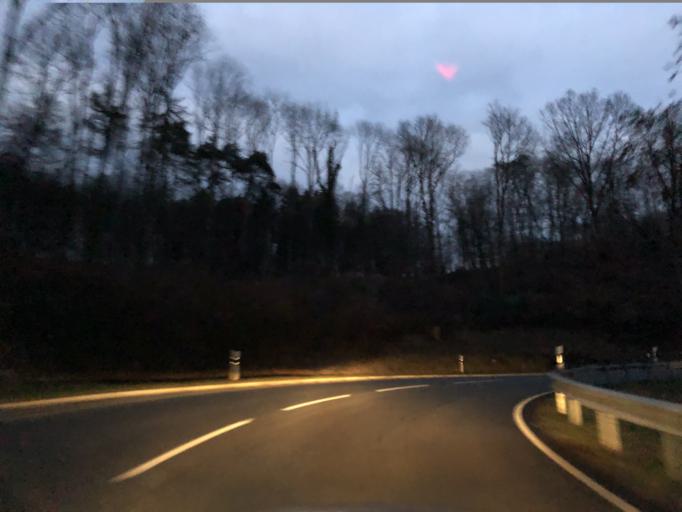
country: DE
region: Rheinland-Pfalz
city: Nassau
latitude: 50.3002
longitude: 7.8075
